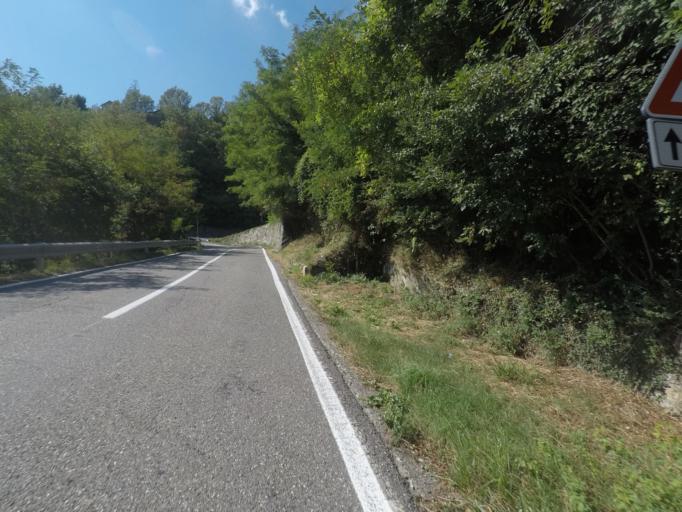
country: IT
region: Tuscany
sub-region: Provincia di Massa-Carrara
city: Fivizzano
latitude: 44.2511
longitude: 10.1751
